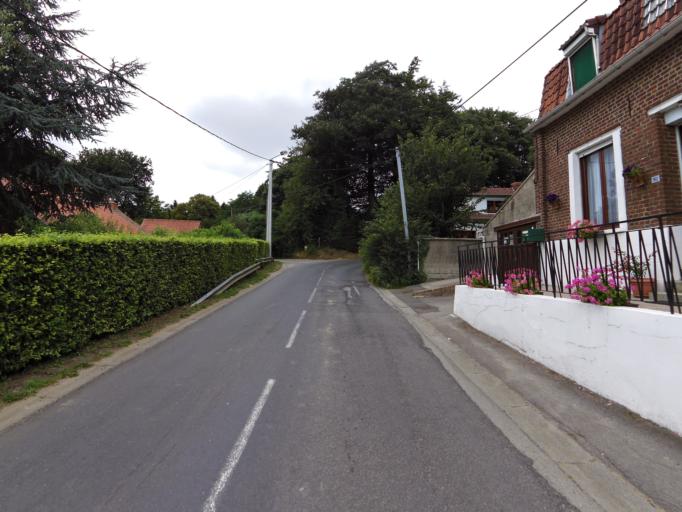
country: FR
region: Nord-Pas-de-Calais
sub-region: Departement du Nord
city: Godewaersvelde
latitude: 50.7854
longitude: 2.6607
